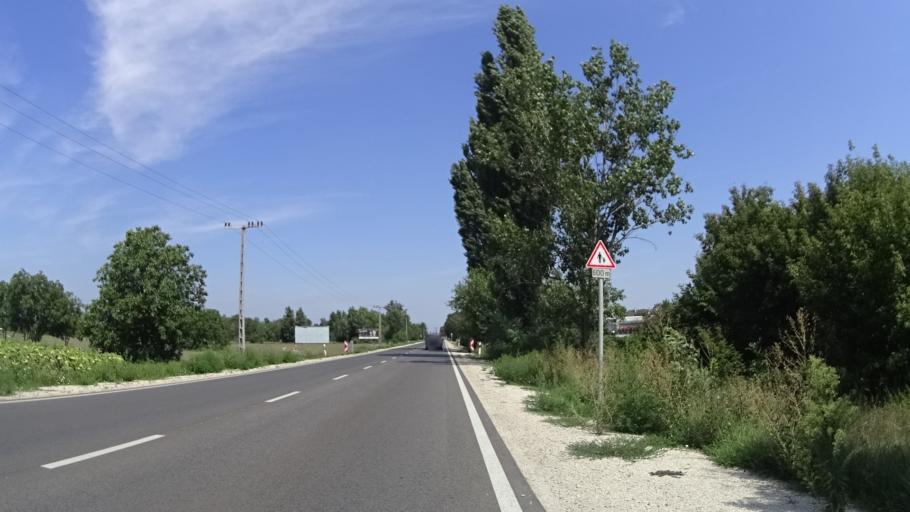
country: HU
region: Fejer
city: Szekesfehervar
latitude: 47.1547
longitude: 18.3991
